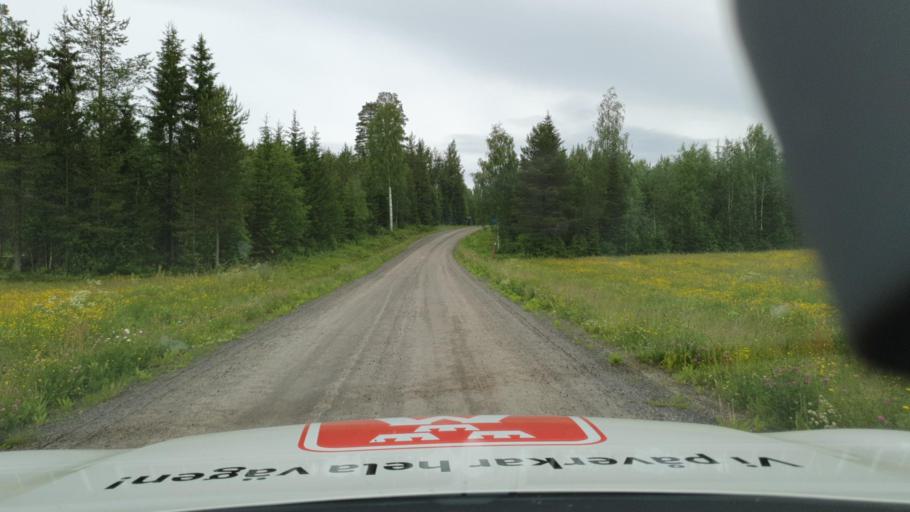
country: SE
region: Vaesterbotten
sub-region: Skelleftea Kommun
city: Burtraesk
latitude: 64.3535
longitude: 20.6130
